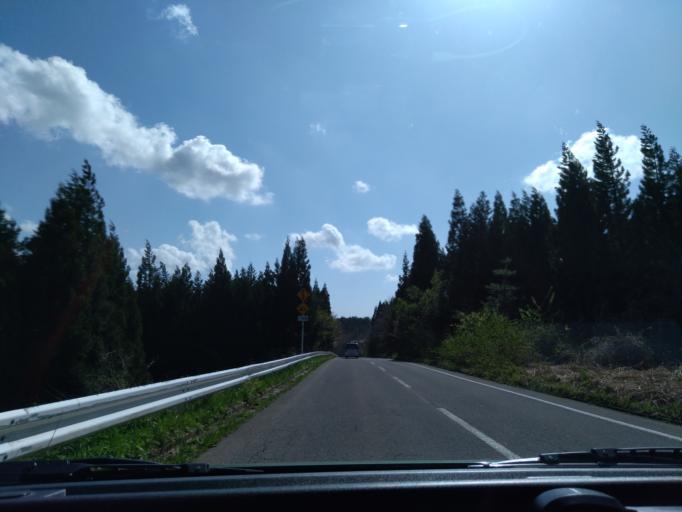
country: JP
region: Akita
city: Akita
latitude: 39.6950
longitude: 140.2494
